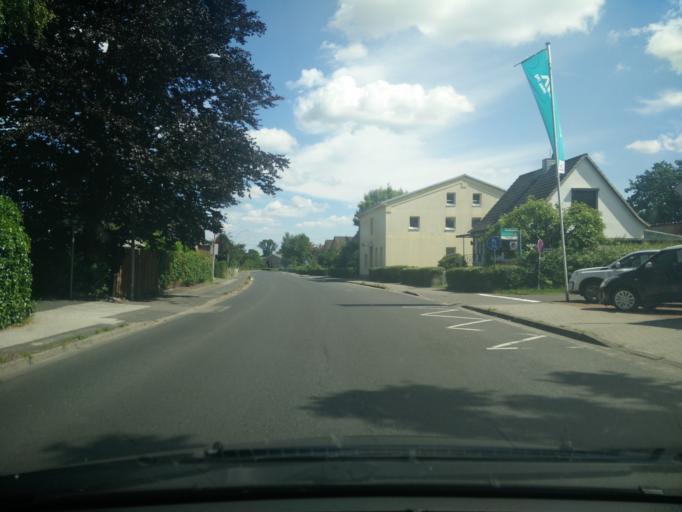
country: DE
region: Schleswig-Holstein
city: Tornesch
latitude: 53.6851
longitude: 9.7292
